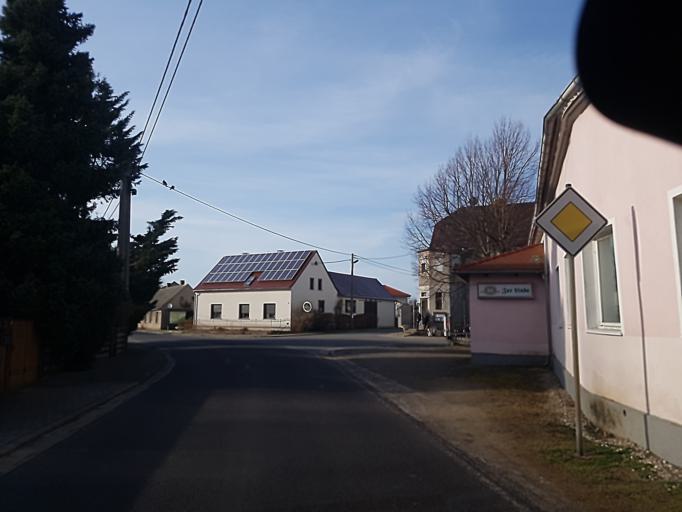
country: DE
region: Brandenburg
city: Falkenberg
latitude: 51.5476
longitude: 13.2939
